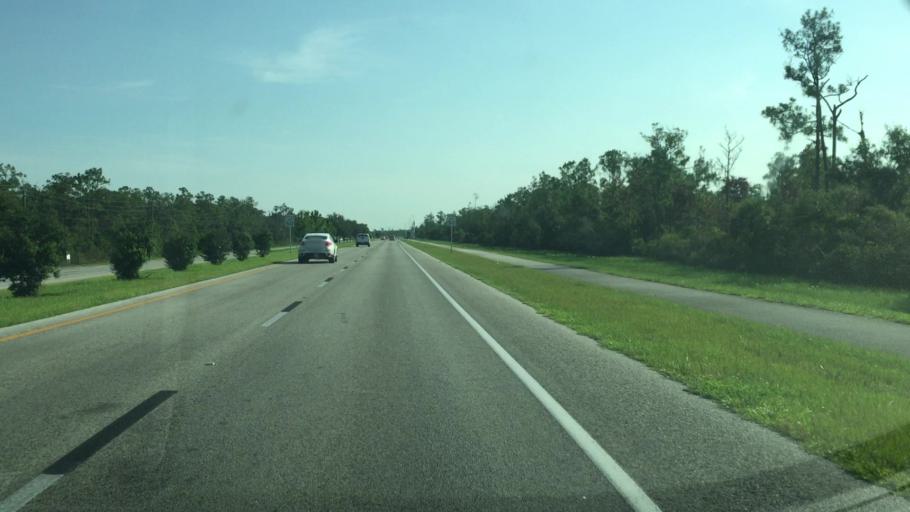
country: US
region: Florida
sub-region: Lee County
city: Villas
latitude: 26.5654
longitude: -81.8298
